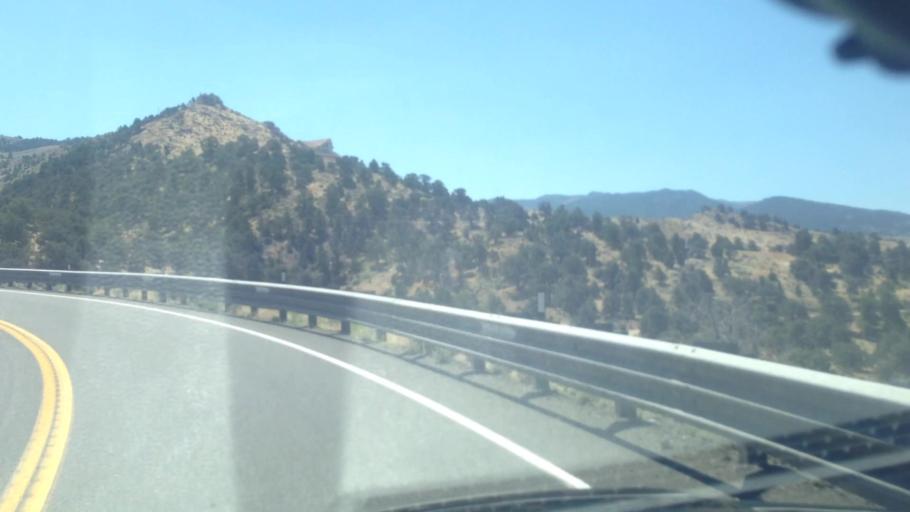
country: US
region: Nevada
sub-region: Storey County
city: Virginia City
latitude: 39.3838
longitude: -119.7136
